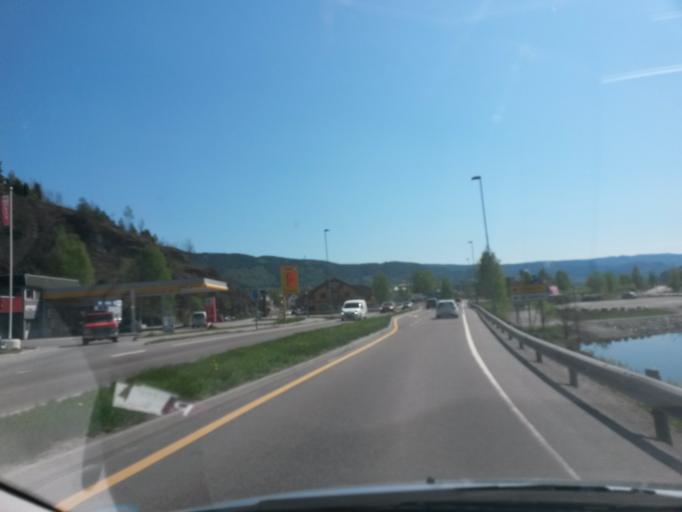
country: NO
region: Telemark
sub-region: Notodden
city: Notodden
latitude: 59.5608
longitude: 9.2469
